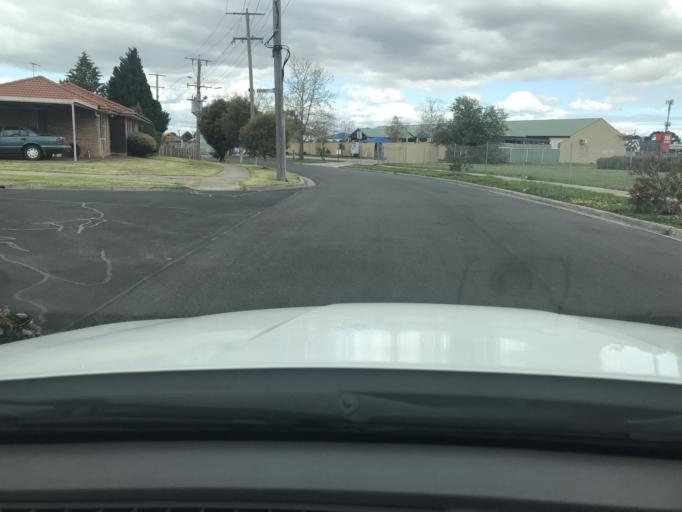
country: AU
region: Victoria
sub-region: Hume
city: Craigieburn
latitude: -37.5948
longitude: 144.9199
